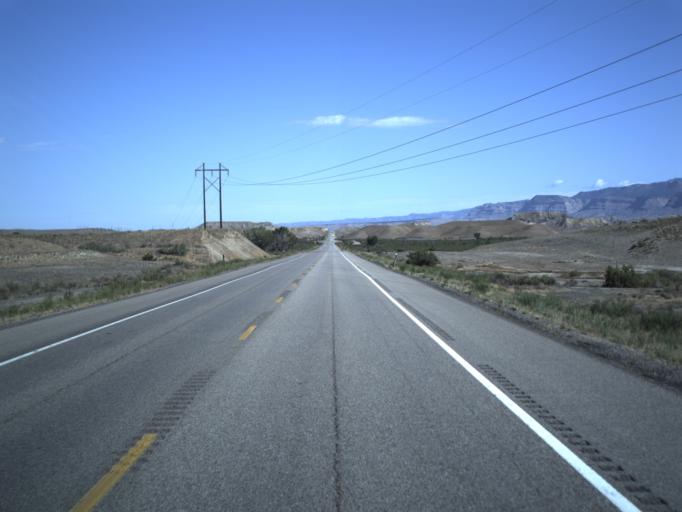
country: US
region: Utah
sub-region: Carbon County
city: East Carbon City
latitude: 39.2572
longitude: -110.3404
